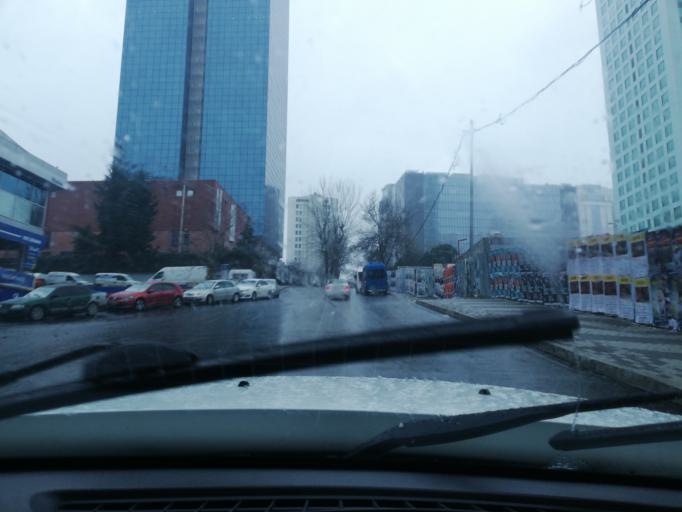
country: TR
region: Istanbul
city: Sisli
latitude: 41.1111
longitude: 29.0202
